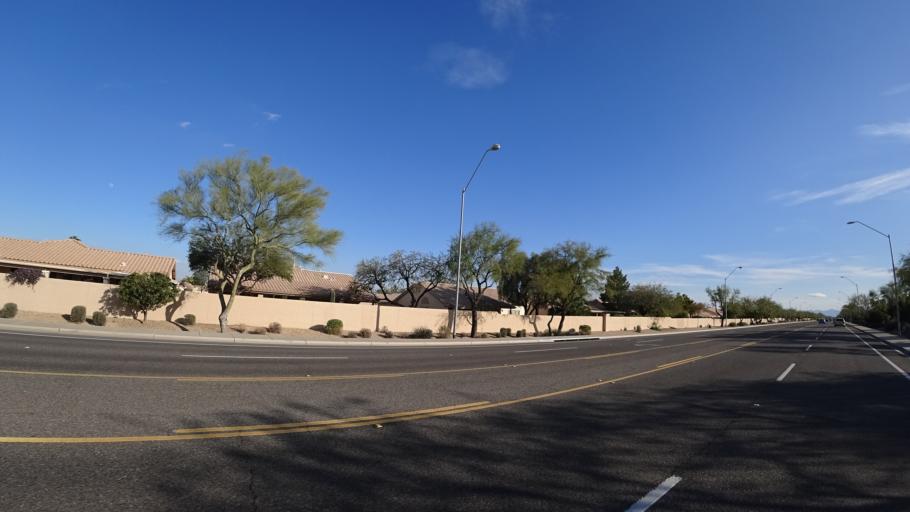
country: US
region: Arizona
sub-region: Maricopa County
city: Sun City
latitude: 33.6624
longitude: -112.2551
